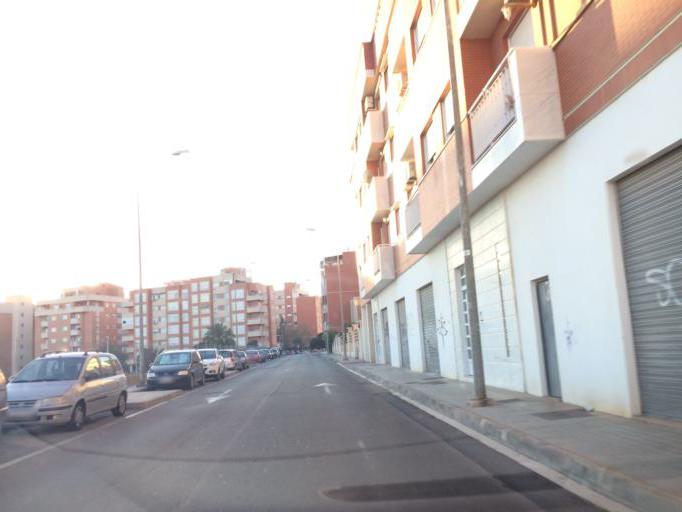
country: ES
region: Andalusia
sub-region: Provincia de Almeria
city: Almeria
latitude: 36.8543
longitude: -2.4436
